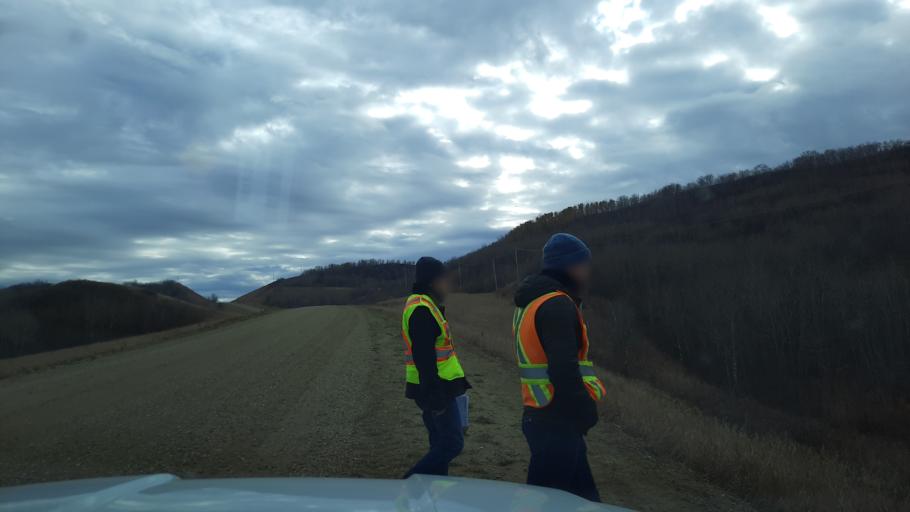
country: CA
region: Saskatchewan
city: Pilot Butte
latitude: 50.7715
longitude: -104.2813
